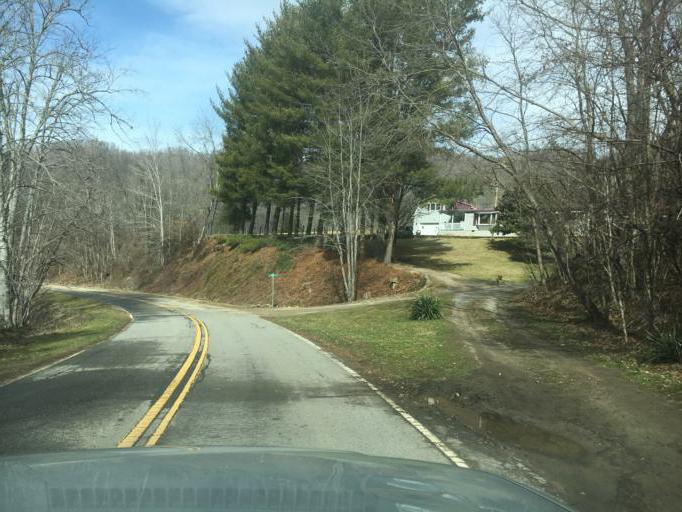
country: US
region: North Carolina
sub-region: Haywood County
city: Canton
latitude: 35.4601
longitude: -82.8406
